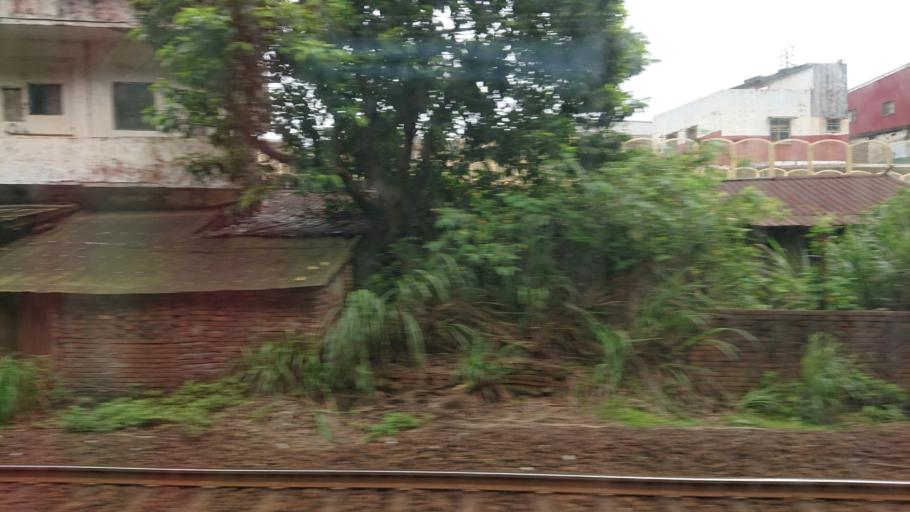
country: TW
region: Taiwan
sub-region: Keelung
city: Keelung
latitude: 25.1073
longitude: 121.8203
